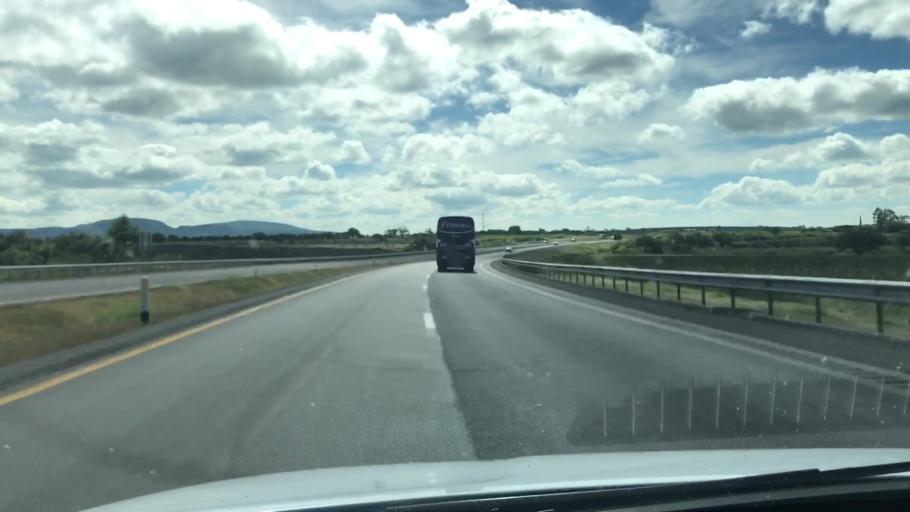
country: MX
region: Guanajuato
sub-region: Irapuato
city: Ex-Hacienda del Copal
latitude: 20.7306
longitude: -101.2923
